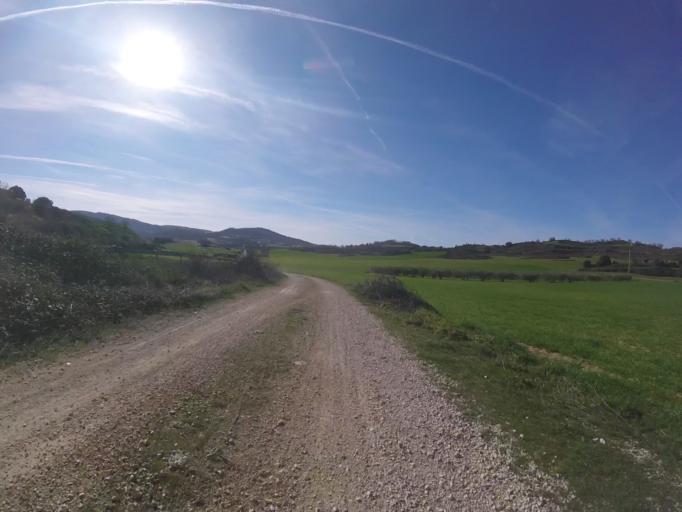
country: ES
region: Navarre
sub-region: Provincia de Navarra
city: Yerri
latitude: 42.6808
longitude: -1.9590
